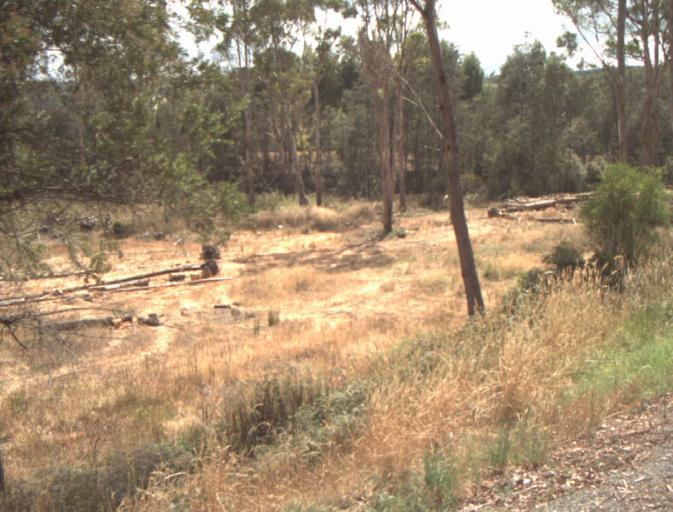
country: AU
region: Tasmania
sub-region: Launceston
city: Mayfield
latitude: -41.2089
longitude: 147.1280
